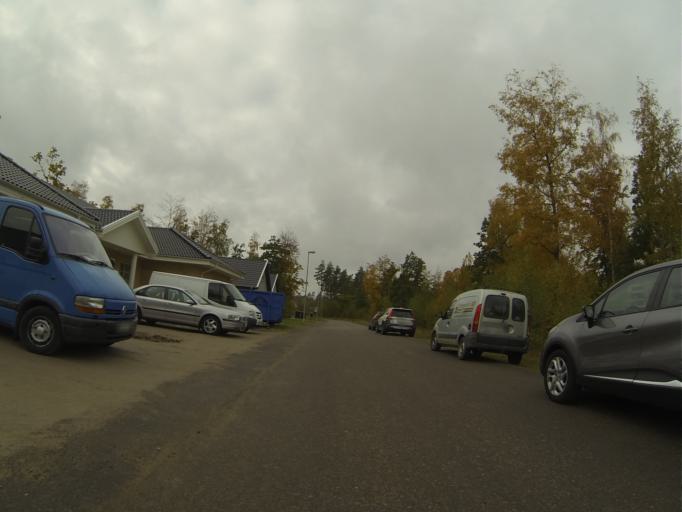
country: SE
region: Skane
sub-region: Sjobo Kommun
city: Sjoebo
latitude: 55.6375
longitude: 13.6740
